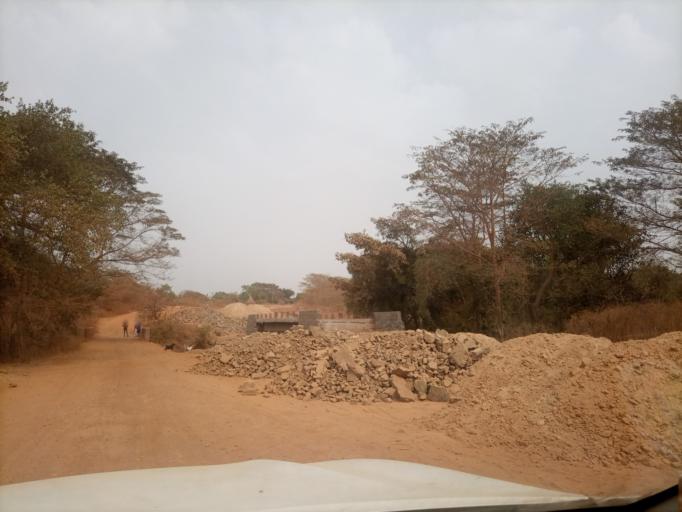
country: ET
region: Oromiya
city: Mendi
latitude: 10.1702
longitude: 35.0932
